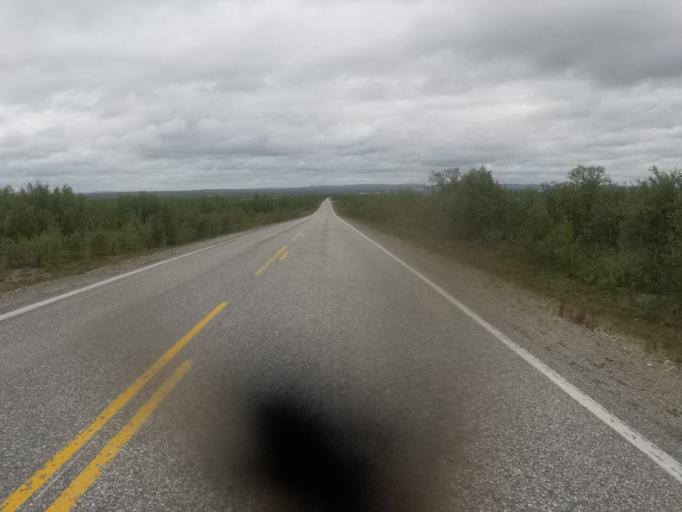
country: NO
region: Finnmark Fylke
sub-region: Kautokeino
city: Kautokeino
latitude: 68.7276
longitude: 23.3084
